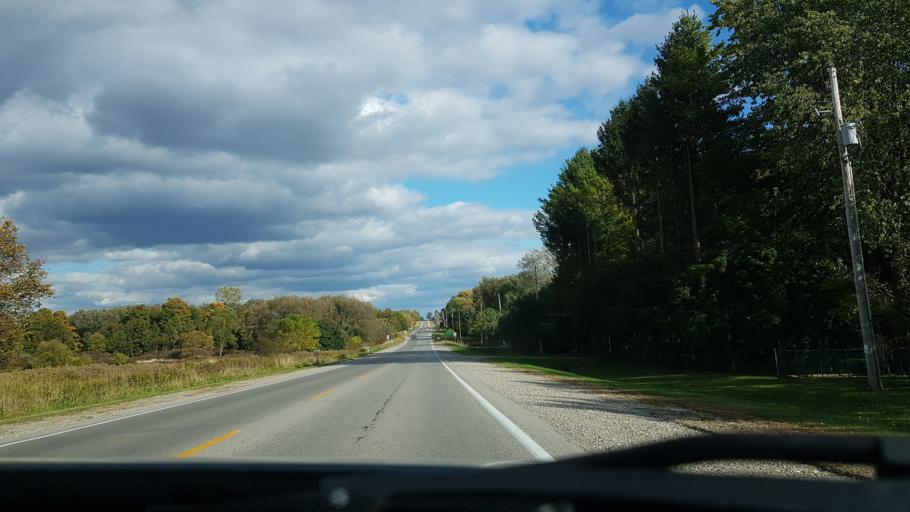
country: CA
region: Ontario
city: Delaware
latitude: 42.9995
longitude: -81.4028
